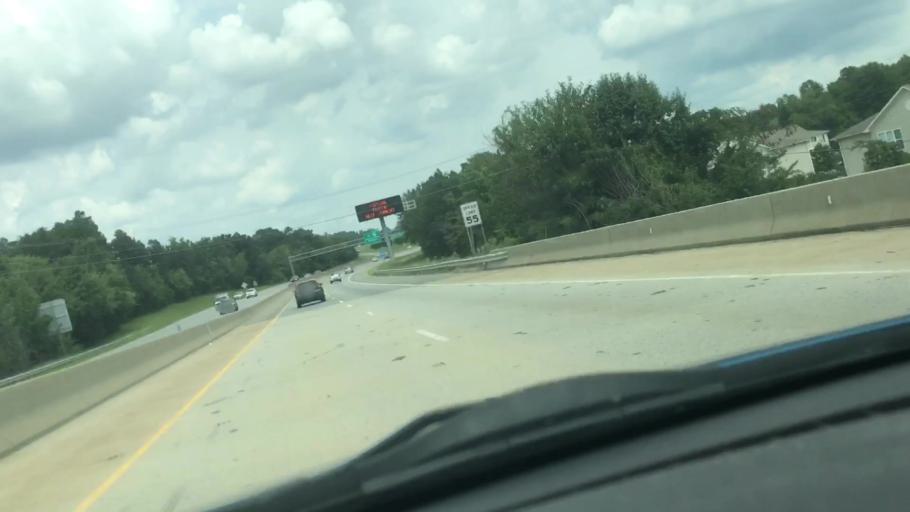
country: US
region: North Carolina
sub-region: Guilford County
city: Greensboro
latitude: 36.0209
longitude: -79.8261
